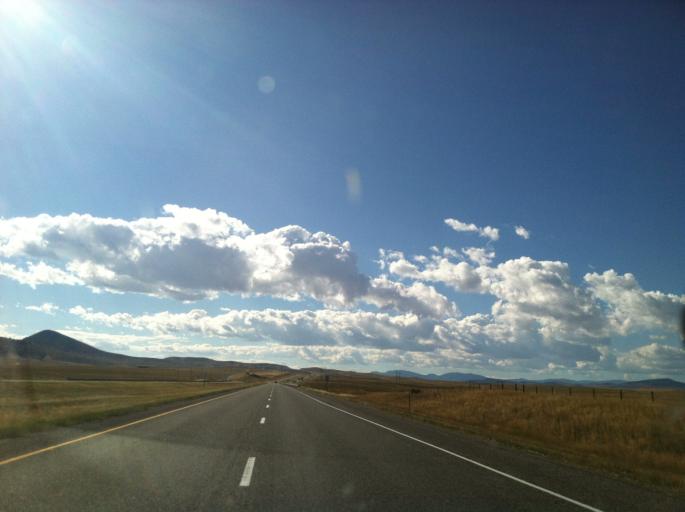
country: US
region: Montana
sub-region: Gallatin County
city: Three Forks
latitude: 45.9185
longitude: -111.6044
